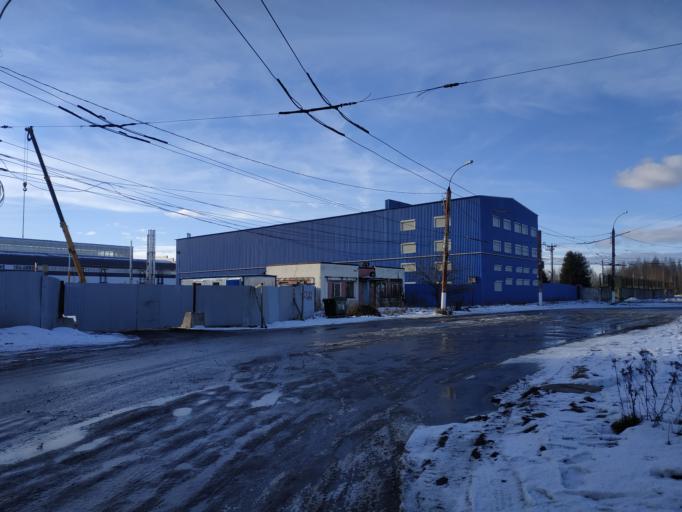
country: RU
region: Tverskaya
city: Tver
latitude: 56.8993
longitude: 35.8230
